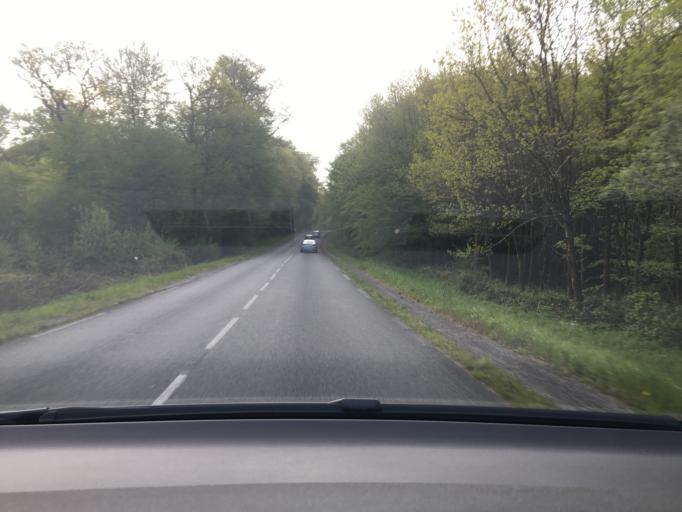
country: FR
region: Franche-Comte
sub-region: Departement du Doubs
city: Courcelles-les-Montbeliard
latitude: 47.4962
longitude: 6.7840
